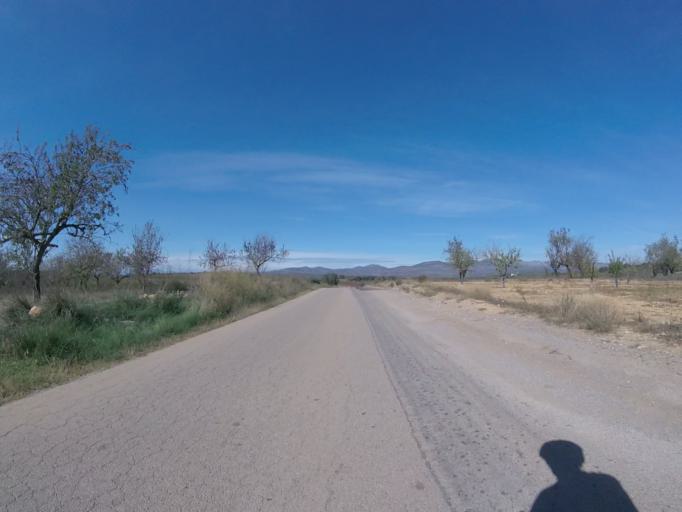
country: ES
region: Valencia
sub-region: Provincia de Castello
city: Benlloch
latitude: 40.2073
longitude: 0.0462
